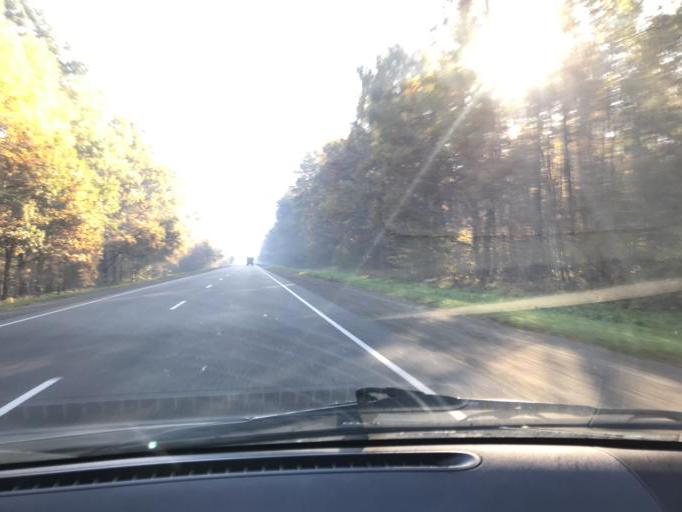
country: BY
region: Brest
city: Horad Luninyets
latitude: 52.2860
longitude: 26.7983
